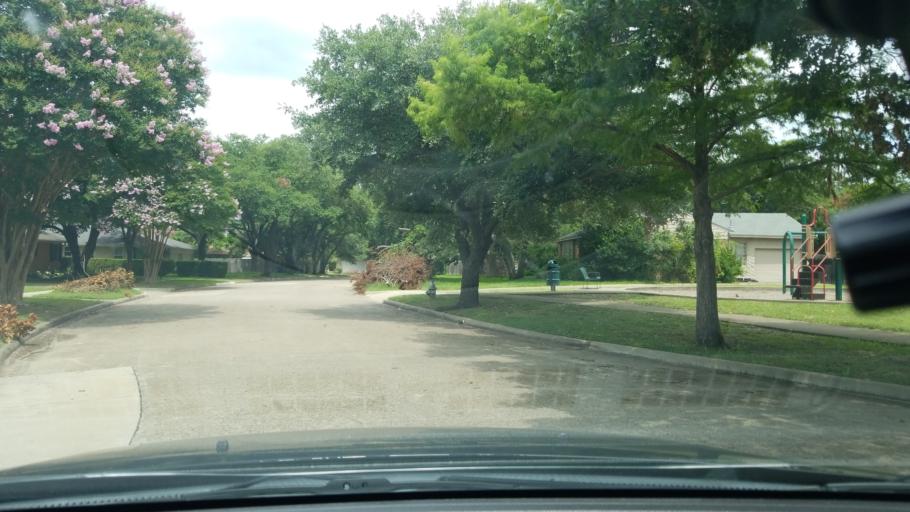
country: US
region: Texas
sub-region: Dallas County
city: Garland
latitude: 32.8294
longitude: -96.6903
